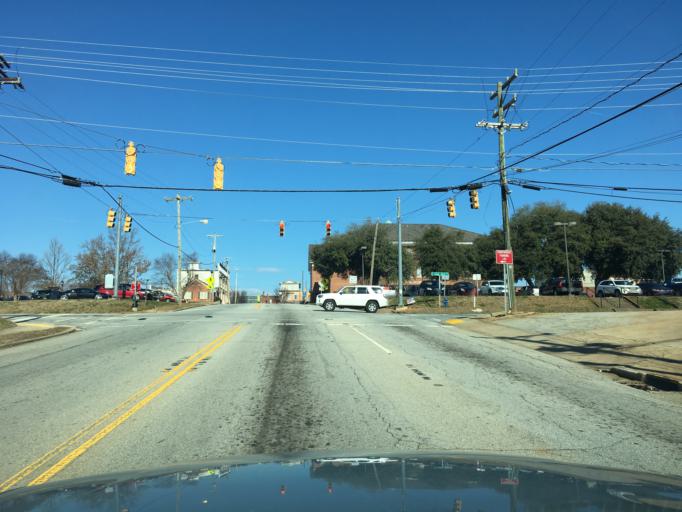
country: US
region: South Carolina
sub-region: Pickens County
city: Pickens
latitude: 34.8822
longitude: -82.7066
